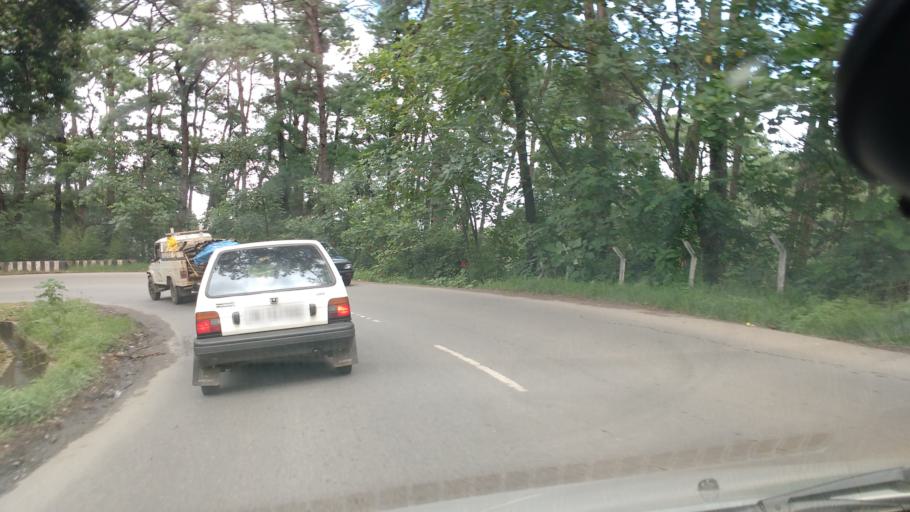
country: IN
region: Meghalaya
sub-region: East Khasi Hills
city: Shillong
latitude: 25.5598
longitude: 91.8525
